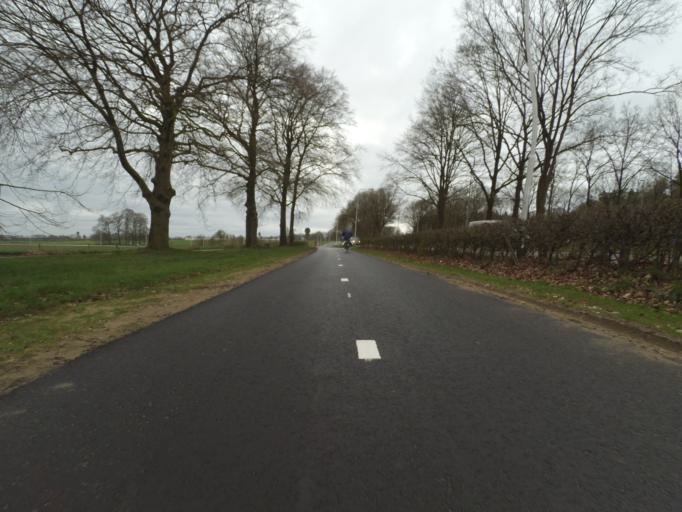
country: NL
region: Gelderland
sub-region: Gemeente Arnhem
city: Arnhem
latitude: 52.0108
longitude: 5.9261
